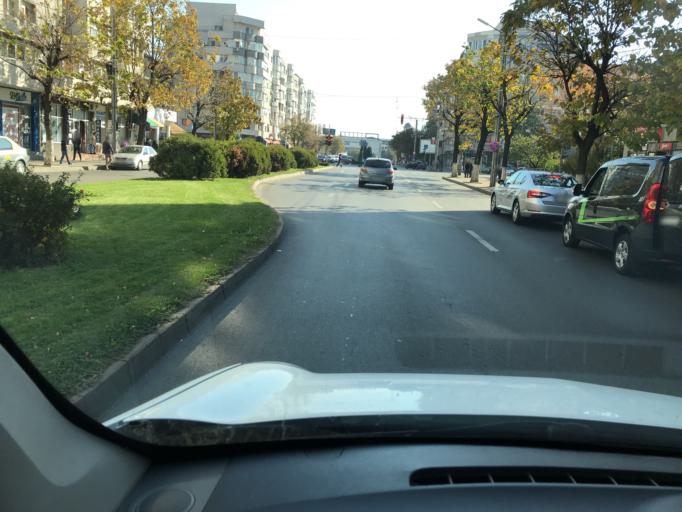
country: RO
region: Olt
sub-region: Municipiul Slatina
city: Slatina
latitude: 44.4269
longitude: 24.3717
